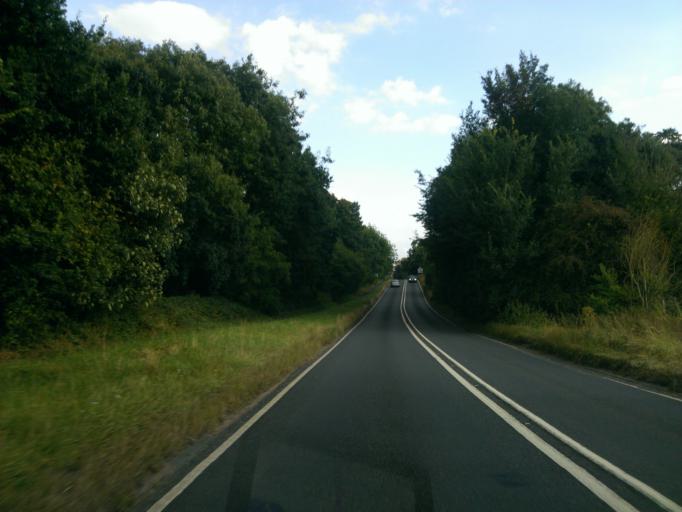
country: GB
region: England
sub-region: Essex
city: Sible Hedingham
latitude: 51.9873
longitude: 0.5862
